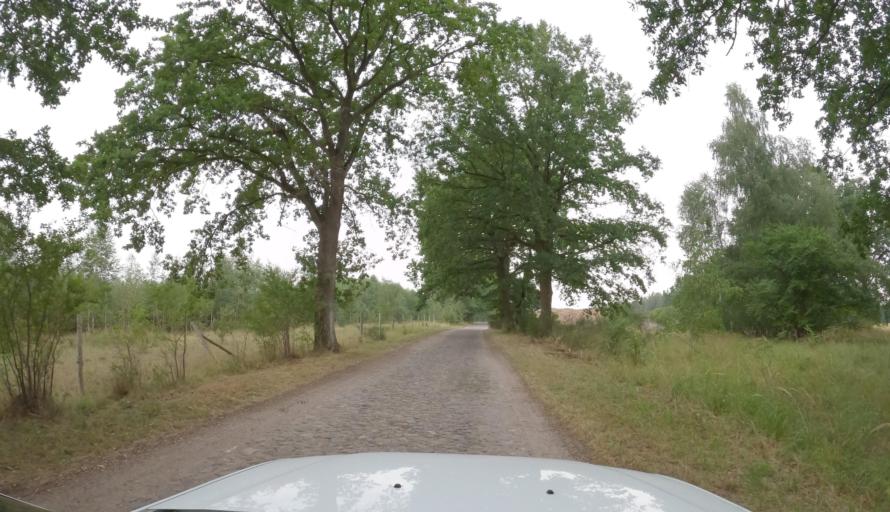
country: PL
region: West Pomeranian Voivodeship
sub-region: Powiat kolobrzeski
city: Ryman
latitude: 53.8508
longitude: 15.5887
